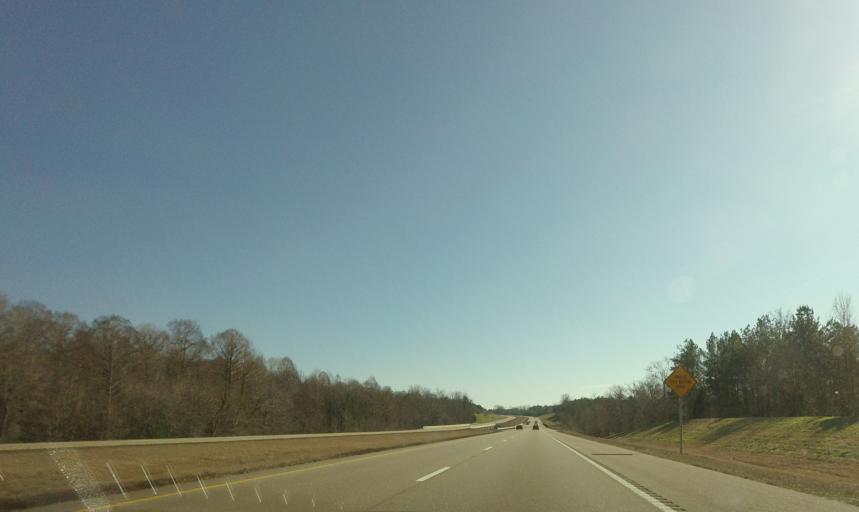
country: US
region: Mississippi
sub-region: Marshall County
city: Holly Springs
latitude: 34.6948
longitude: -89.3909
